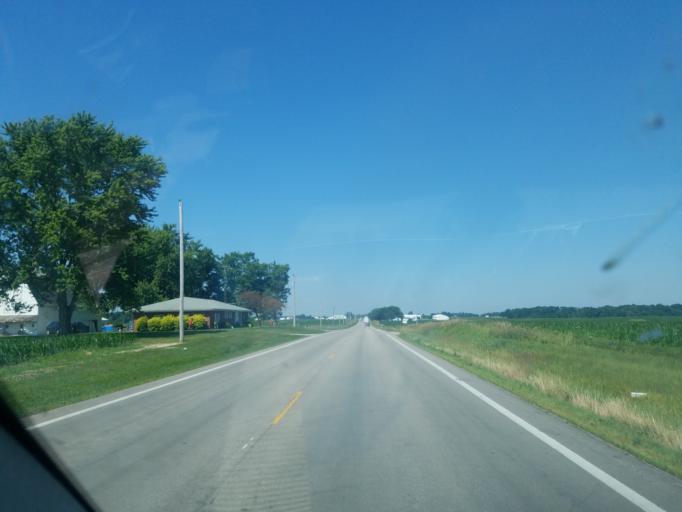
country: US
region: Ohio
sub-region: Shelby County
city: Botkins
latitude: 40.4388
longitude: -84.2332
